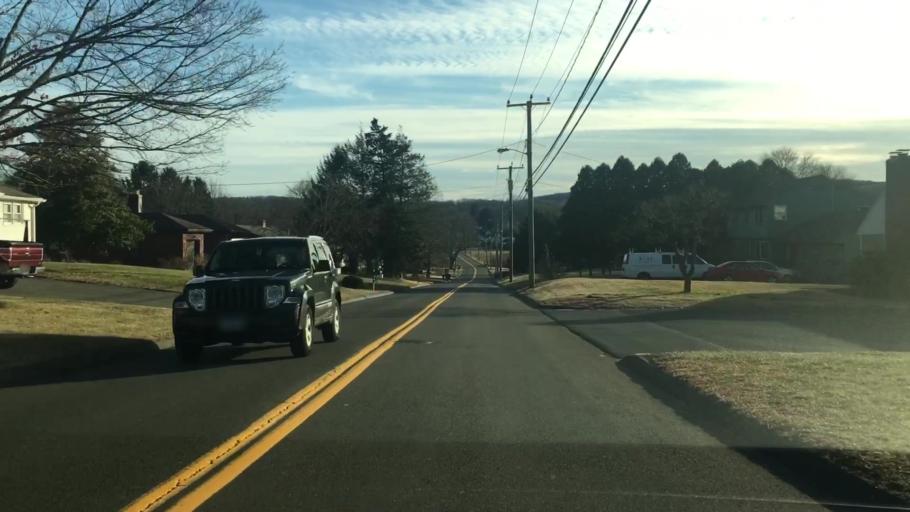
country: US
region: Connecticut
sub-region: Middlesex County
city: Middletown
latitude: 41.5303
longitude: -72.6505
